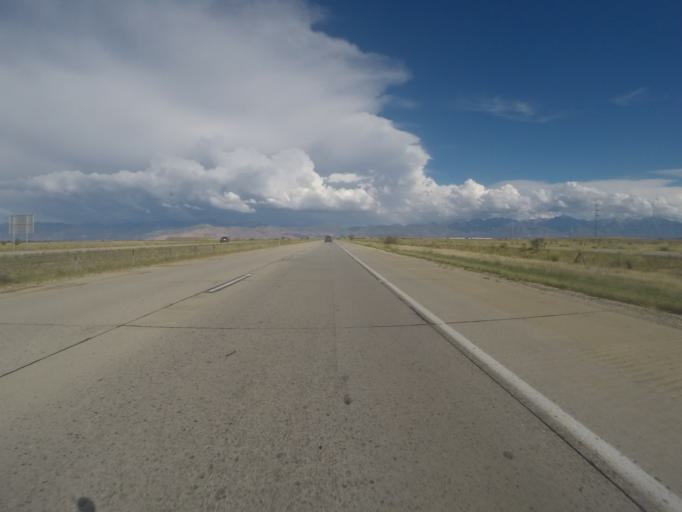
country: US
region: Utah
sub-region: Salt Lake County
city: Magna
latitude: 40.7708
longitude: -112.0844
